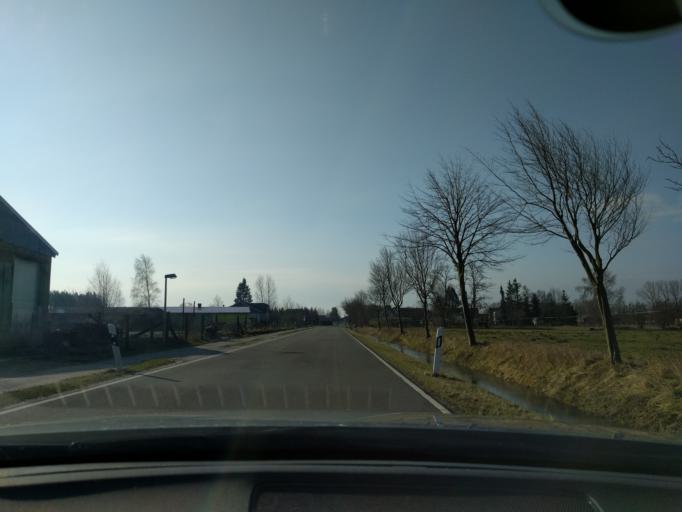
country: DE
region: Saxony-Anhalt
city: Hohenberg-Krusemark
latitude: 52.7291
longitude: 11.9463
